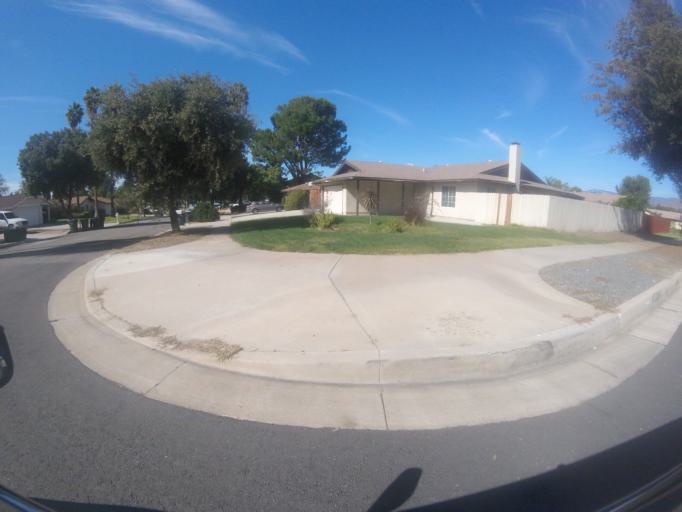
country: US
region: California
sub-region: San Bernardino County
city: Mentone
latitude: 34.0672
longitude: -117.1520
